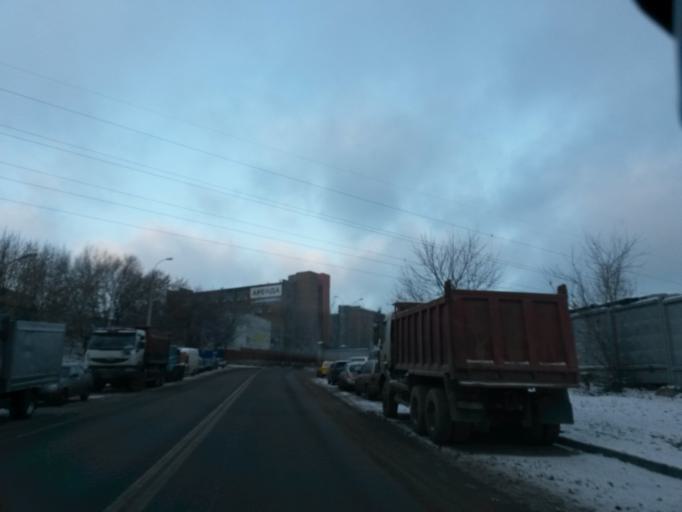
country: RU
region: Moscow
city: Amin'yevo
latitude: 55.7039
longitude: 37.4505
